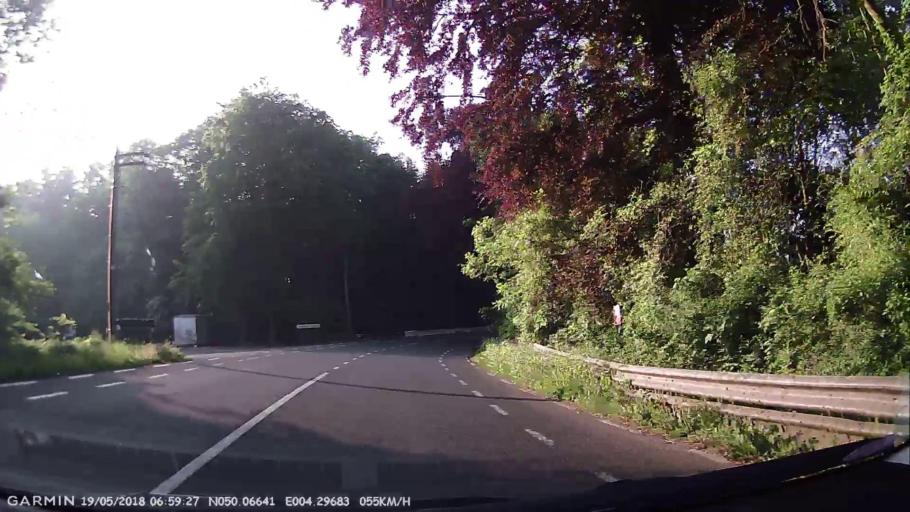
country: BE
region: Wallonia
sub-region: Province du Hainaut
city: Chimay
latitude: 50.0663
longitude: 4.2971
